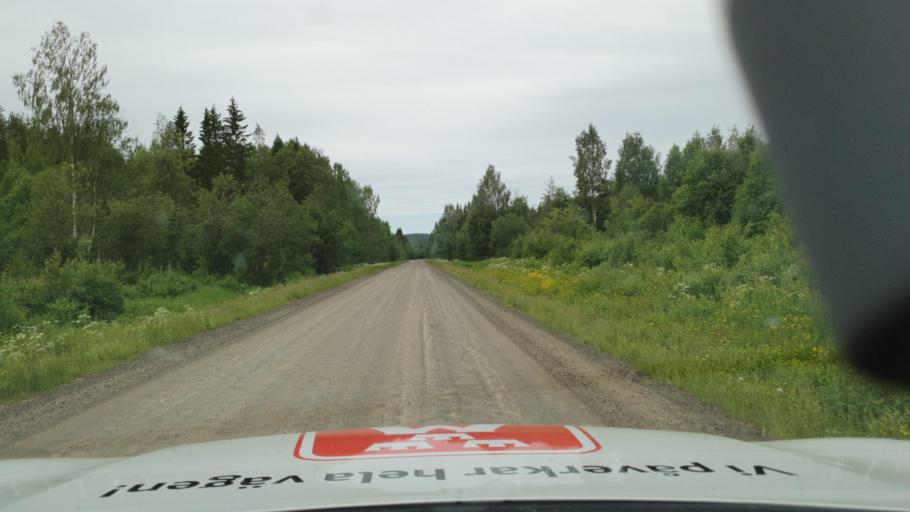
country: SE
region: Vaesterbotten
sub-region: Skelleftea Kommun
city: Burtraesk
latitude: 64.3283
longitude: 20.6261
